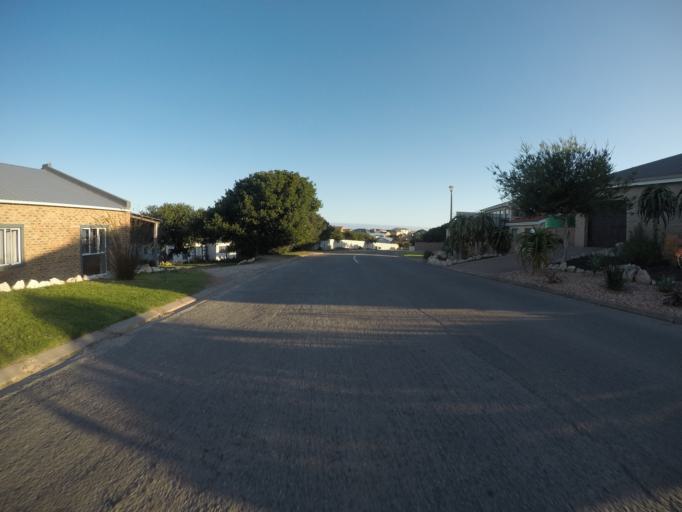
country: ZA
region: Western Cape
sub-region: Eden District Municipality
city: Riversdale
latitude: -34.3843
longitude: 21.4028
